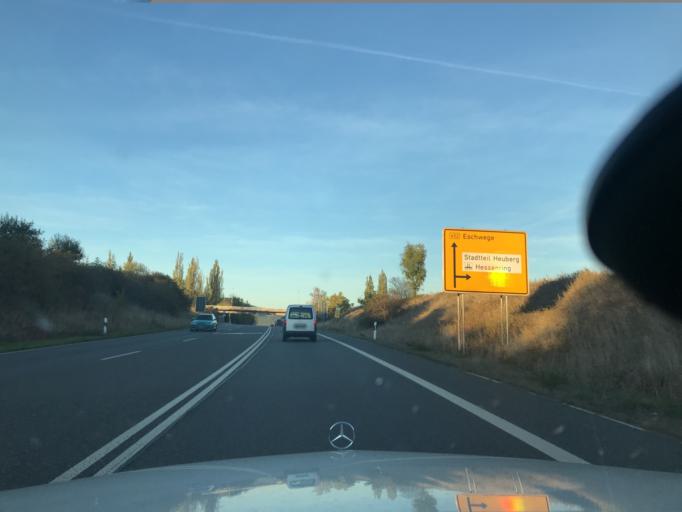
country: DE
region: Hesse
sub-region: Regierungsbezirk Kassel
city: Eschwege
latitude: 51.1752
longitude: 10.0326
